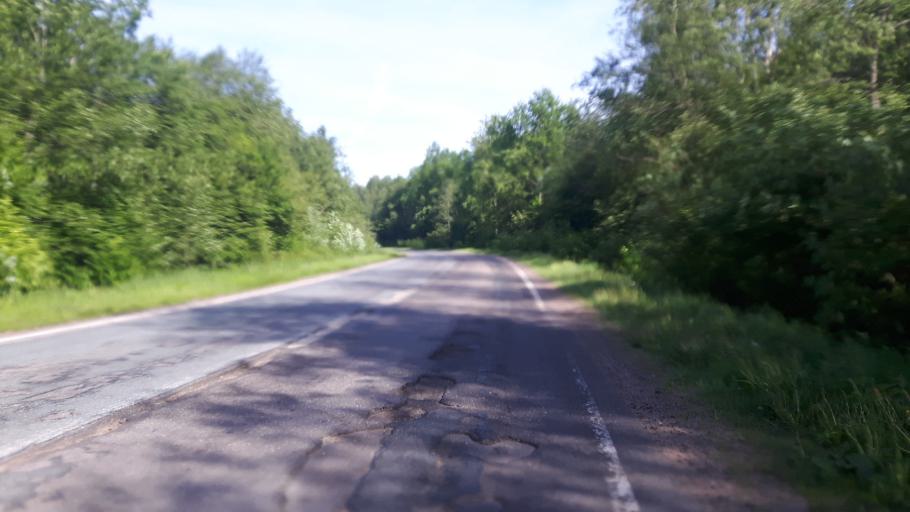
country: RU
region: Leningrad
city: Ivangorod
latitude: 59.4166
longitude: 28.3681
